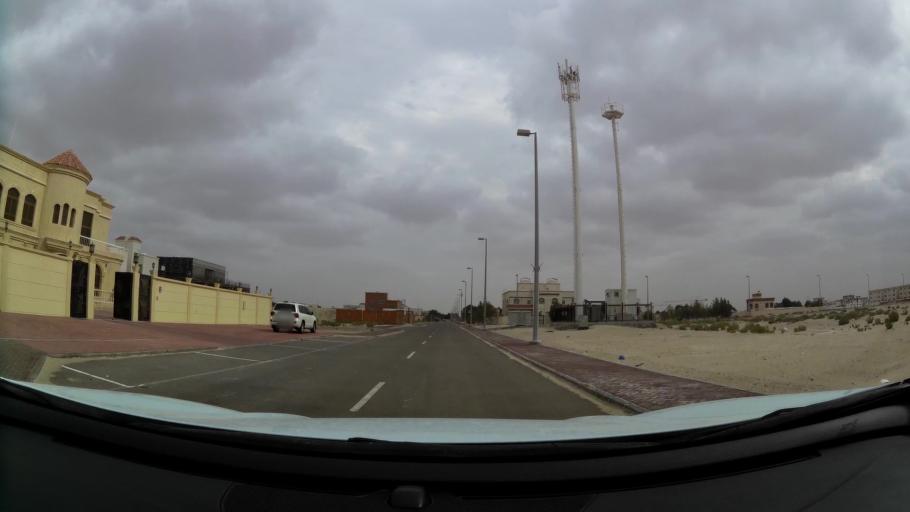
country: AE
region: Abu Dhabi
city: Abu Dhabi
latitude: 24.3790
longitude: 54.6366
